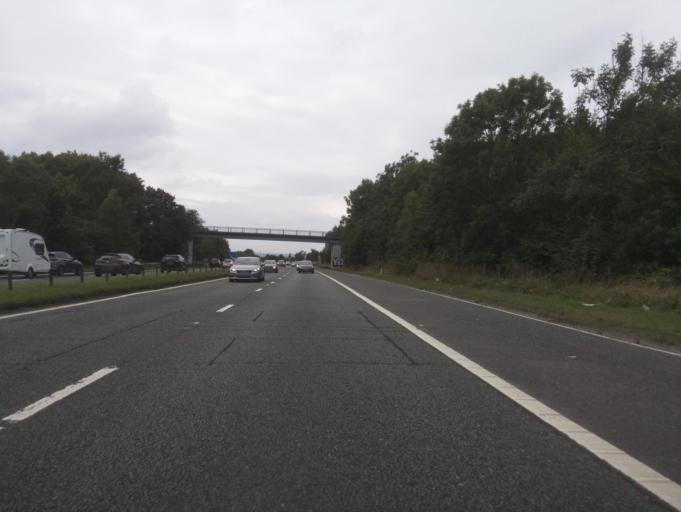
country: GB
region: England
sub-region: County Durham
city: Chester-le-Street
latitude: 54.8525
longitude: -1.5365
